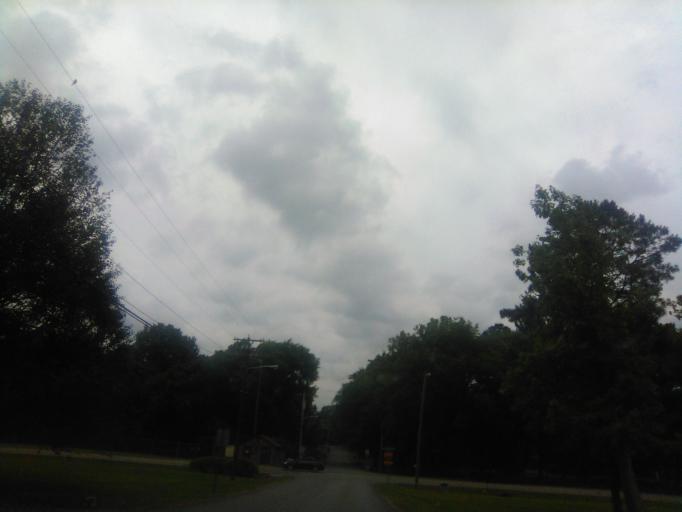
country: US
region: Tennessee
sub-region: Davidson County
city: Belle Meade
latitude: 36.1054
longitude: -86.8794
